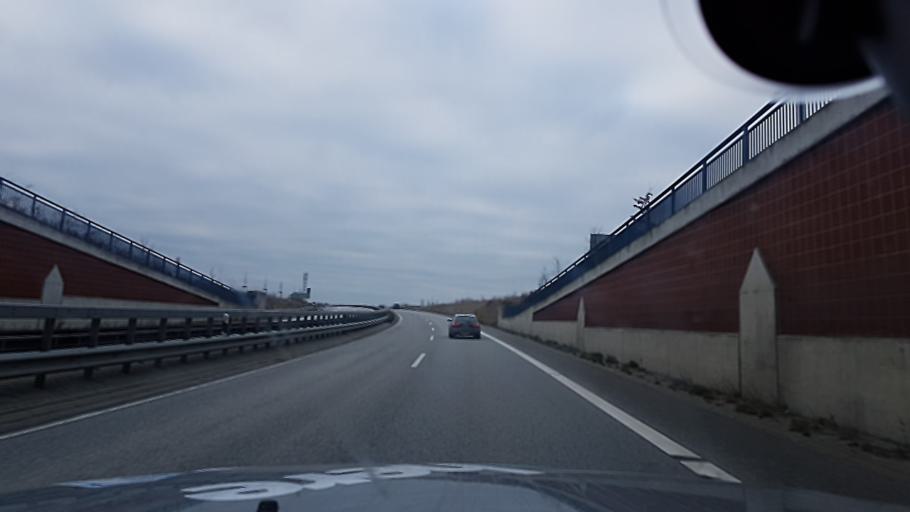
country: DE
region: Schleswig-Holstein
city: Gremersdorf
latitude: 54.3314
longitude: 10.9332
